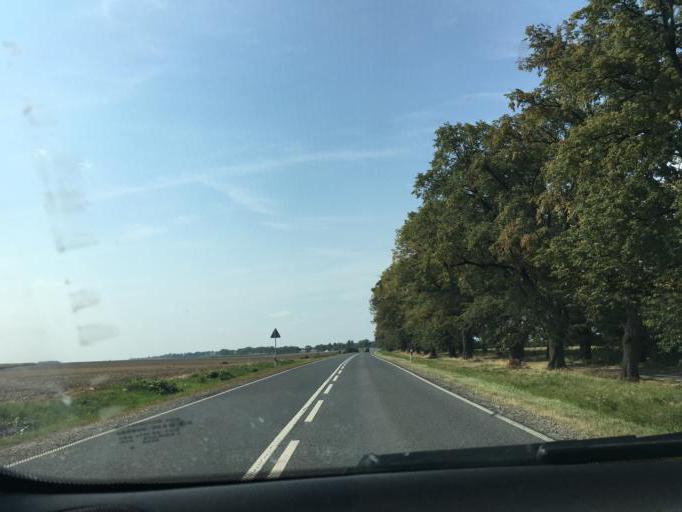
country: PL
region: Opole Voivodeship
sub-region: Powiat prudnicki
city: Laka Prudnicka
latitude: 50.4138
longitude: 17.4926
